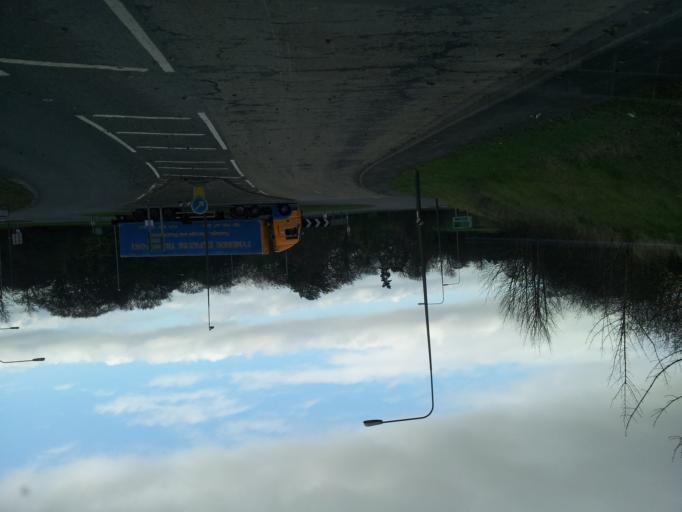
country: GB
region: England
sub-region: Lincolnshire
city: Louth
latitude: 53.3650
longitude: -0.0275
